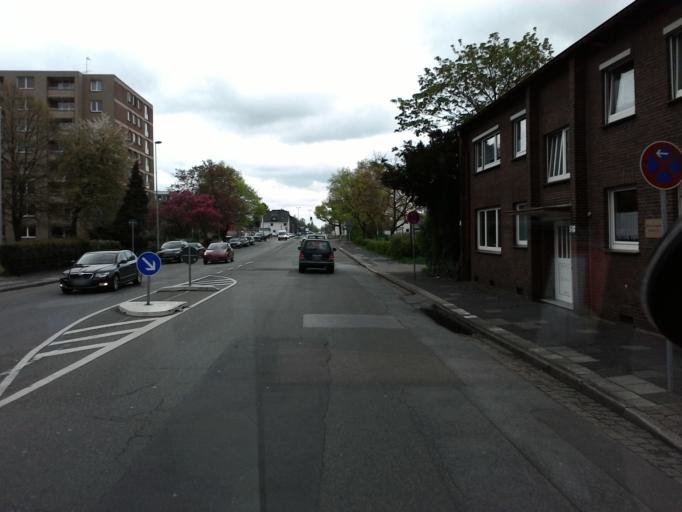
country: DE
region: North Rhine-Westphalia
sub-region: Regierungsbezirk Dusseldorf
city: Moers
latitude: 51.4481
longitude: 6.6586
